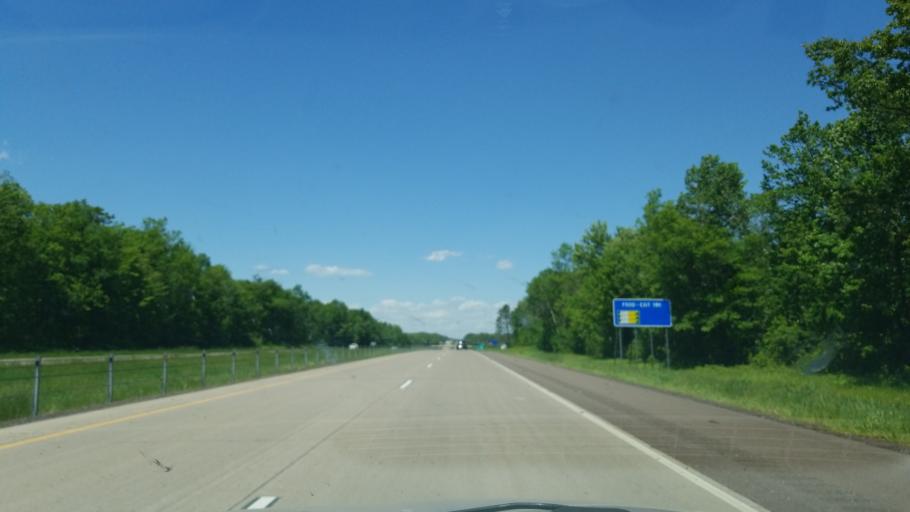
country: US
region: Minnesota
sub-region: Pine County
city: Sandstone
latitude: 46.1159
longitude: -92.8878
